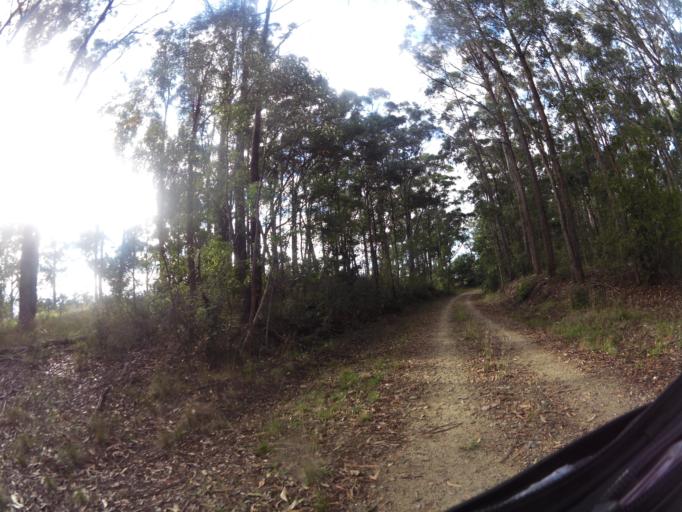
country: AU
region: Victoria
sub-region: East Gippsland
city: Lakes Entrance
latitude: -37.7326
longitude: 148.4272
